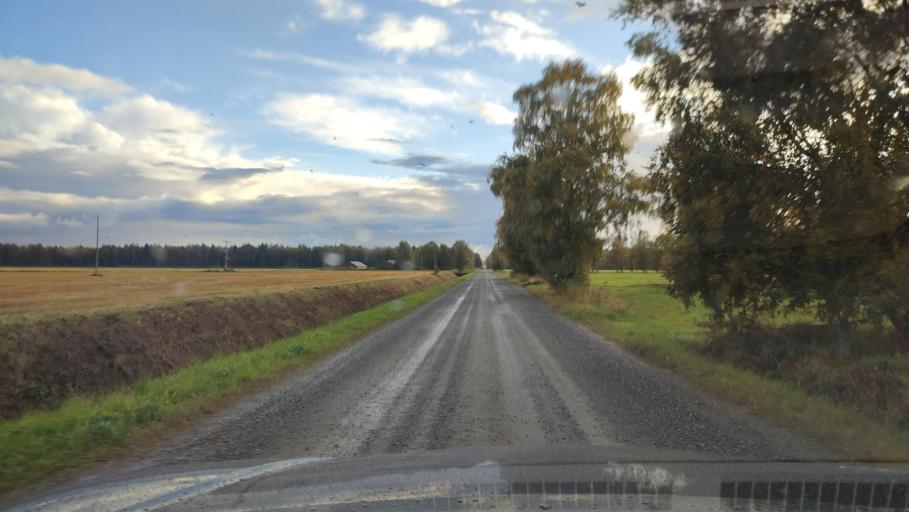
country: FI
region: Southern Ostrobothnia
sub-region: Suupohja
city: Karijoki
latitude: 62.3247
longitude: 21.5729
